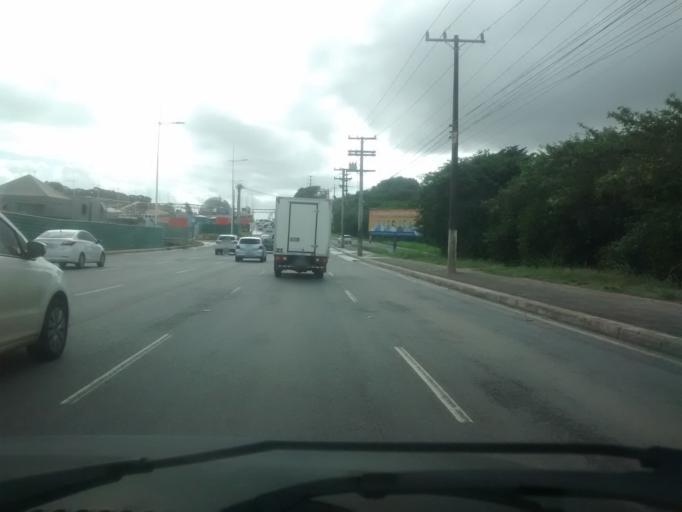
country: BR
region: Bahia
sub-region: Salvador
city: Salvador
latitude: -12.9602
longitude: -38.4320
